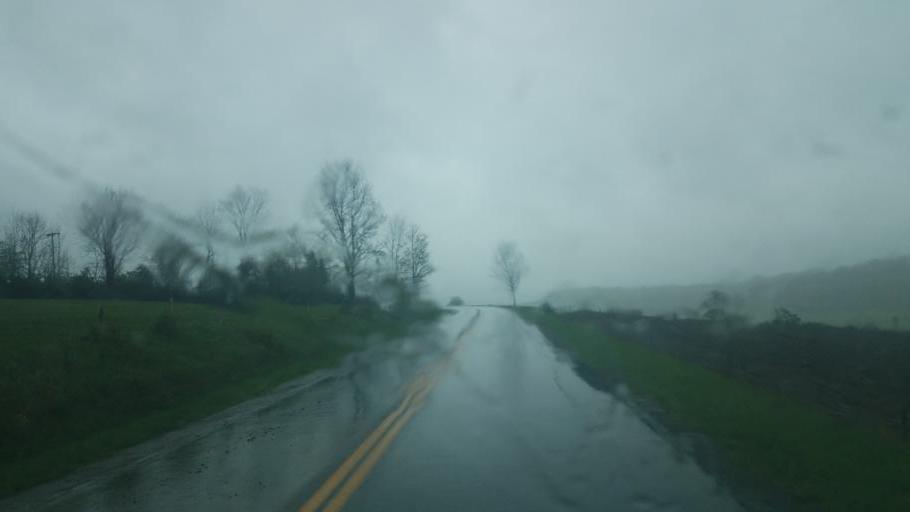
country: US
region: Pennsylvania
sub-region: Tioga County
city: Elkland
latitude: 42.0802
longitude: -77.4310
